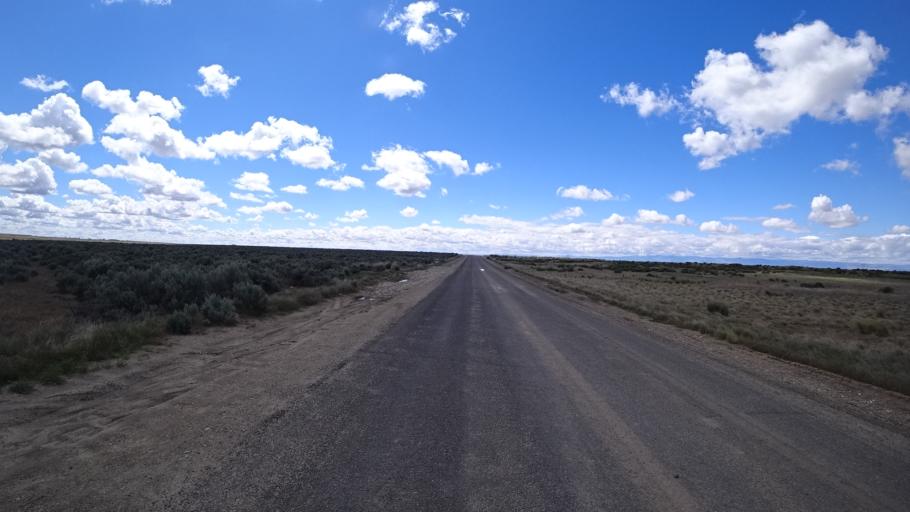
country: US
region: Idaho
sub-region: Ada County
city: Garden City
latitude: 43.4845
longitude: -116.2743
